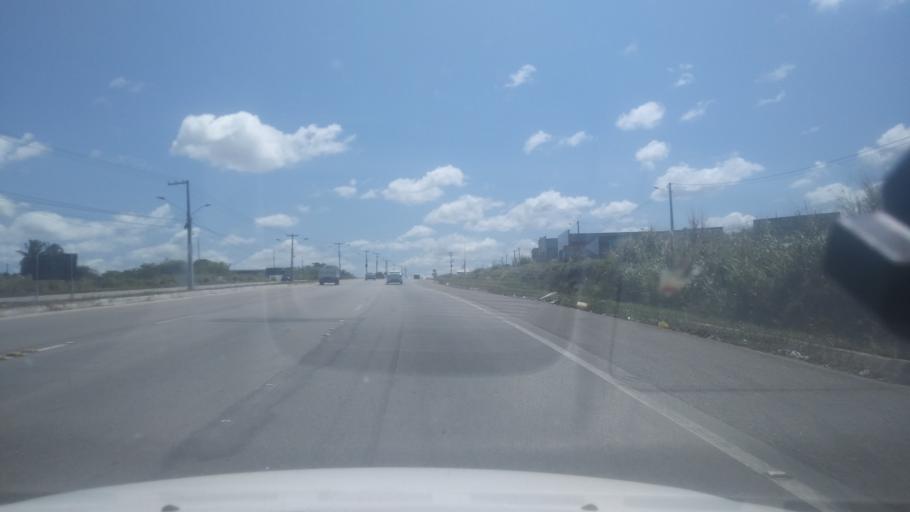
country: BR
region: Rio Grande do Norte
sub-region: Sao Goncalo Do Amarante
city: Sao Goncalo do Amarante
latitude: -5.7572
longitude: -35.3024
